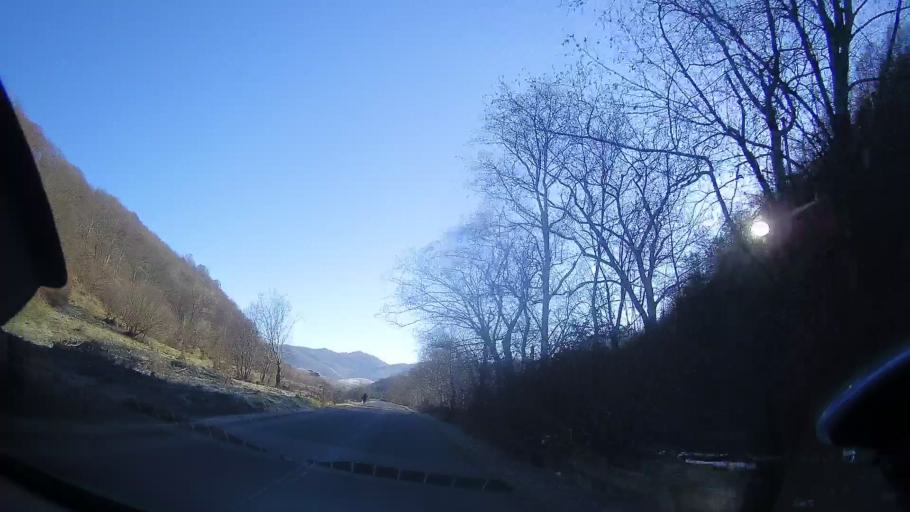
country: RO
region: Cluj
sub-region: Comuna Sacueu
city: Sacuieu
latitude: 46.8323
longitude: 22.8661
